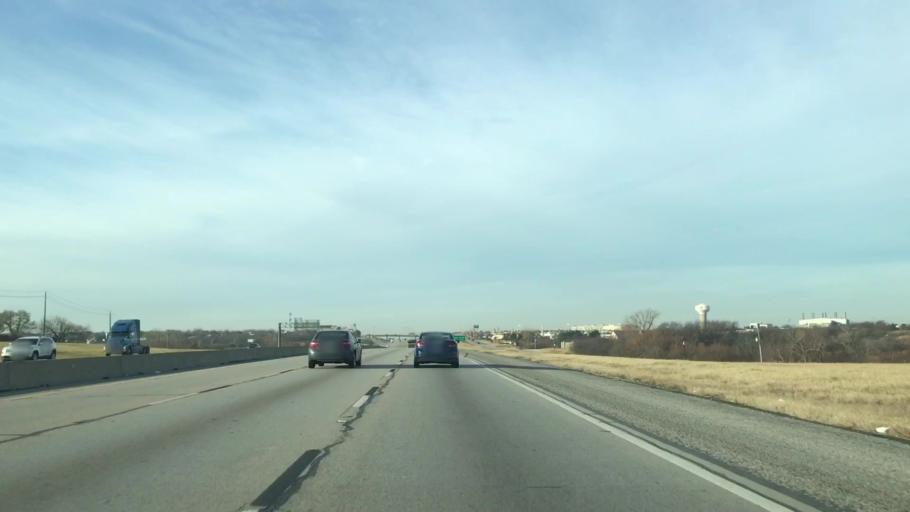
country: US
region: Texas
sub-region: Tarrant County
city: Sansom Park
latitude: 32.8207
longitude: -97.3985
